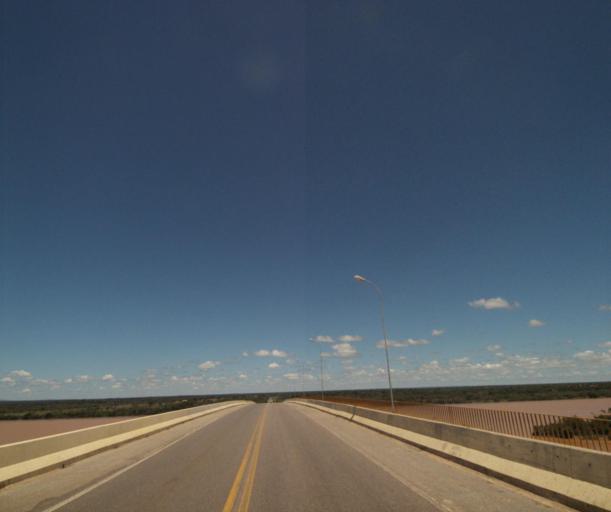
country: BR
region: Bahia
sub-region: Carinhanha
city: Carinhanha
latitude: -14.3259
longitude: -43.7680
